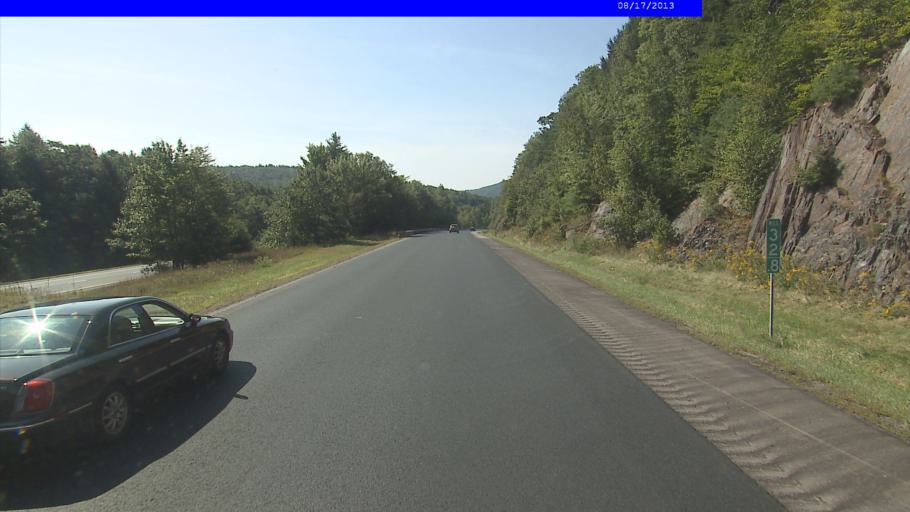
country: US
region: Vermont
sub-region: Windham County
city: Bellows Falls
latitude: 43.1471
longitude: -72.4749
